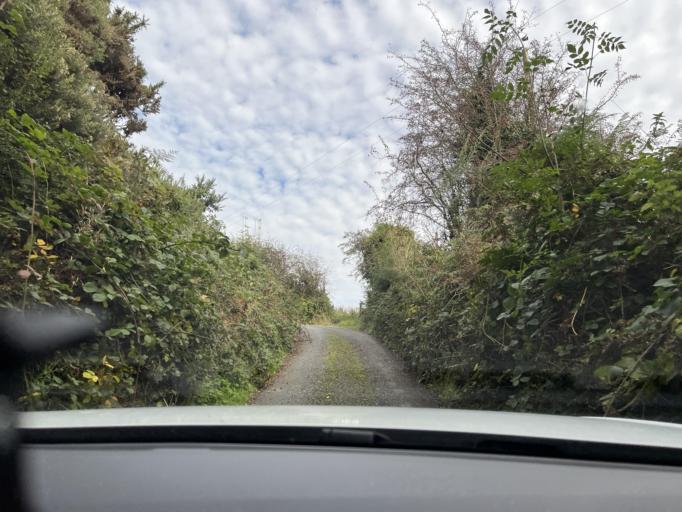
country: IE
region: Connaught
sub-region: Sligo
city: Ballymote
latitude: 54.0501
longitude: -8.4300
